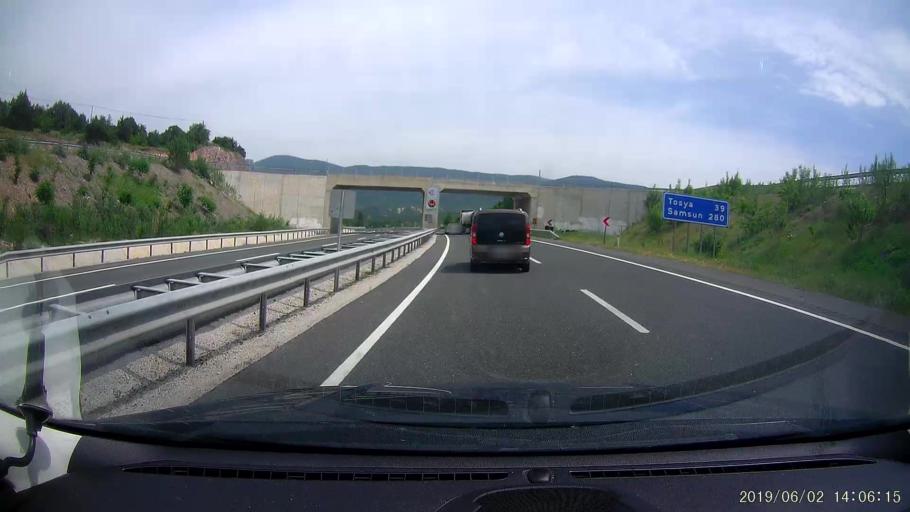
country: TR
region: Cankiri
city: Ilgaz
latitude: 40.8909
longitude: 33.6780
